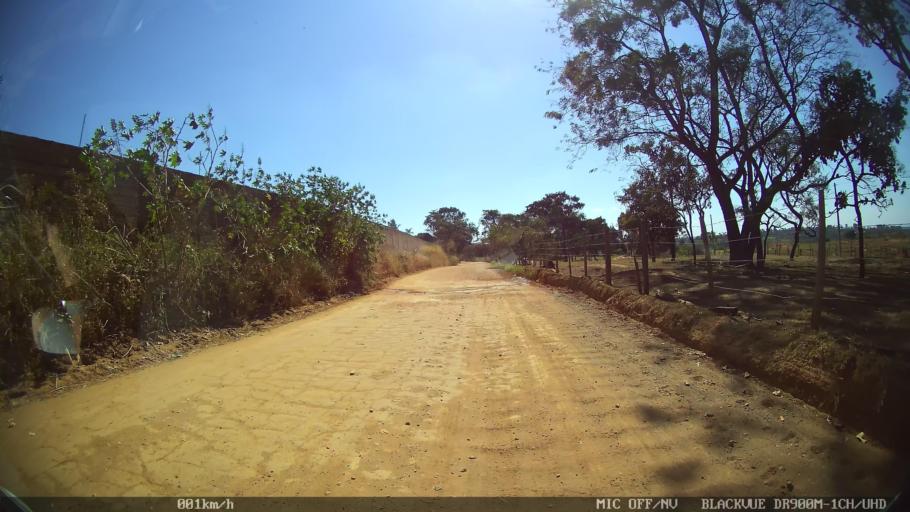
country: BR
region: Sao Paulo
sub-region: Franca
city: Franca
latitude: -20.4570
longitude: -47.4139
